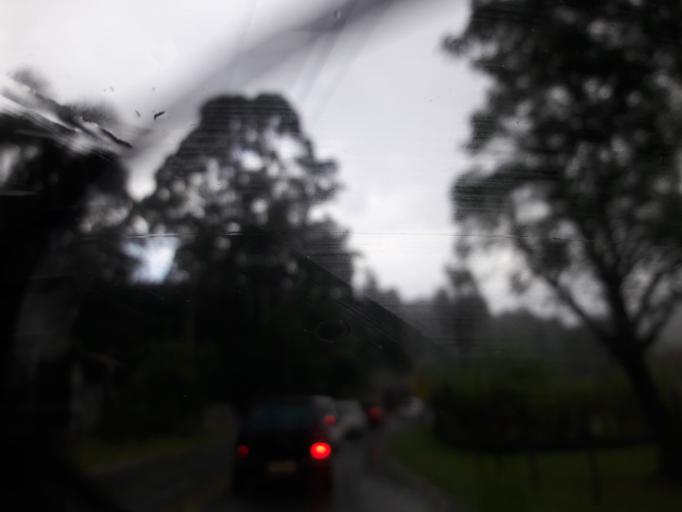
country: BR
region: Sao Paulo
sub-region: Bom Jesus Dos Perdoes
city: Bom Jesus dos Perdoes
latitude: -23.2615
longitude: -46.4176
